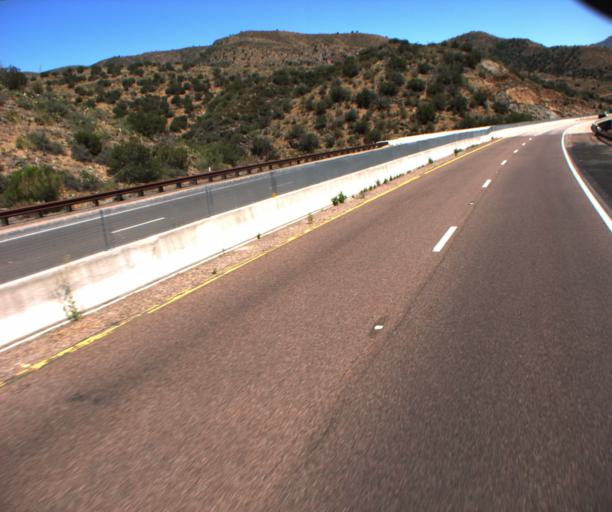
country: US
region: Arizona
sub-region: Gila County
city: Tonto Basin
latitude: 33.8939
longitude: -111.4559
